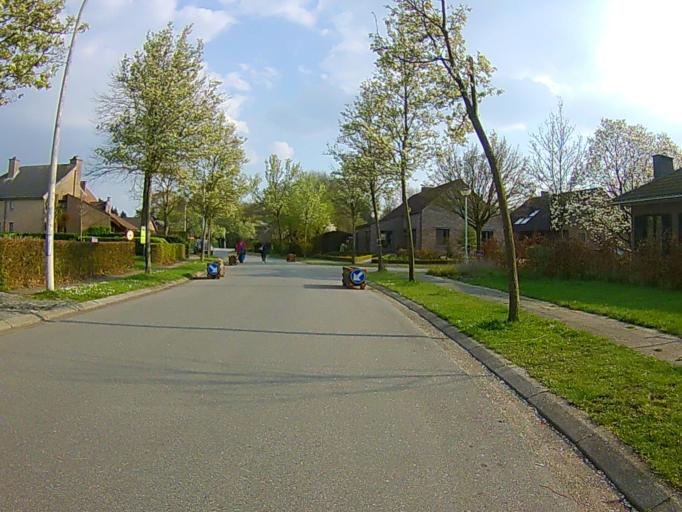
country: BE
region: Flanders
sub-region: Provincie Antwerpen
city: Kalmthout
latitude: 51.3805
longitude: 4.4706
